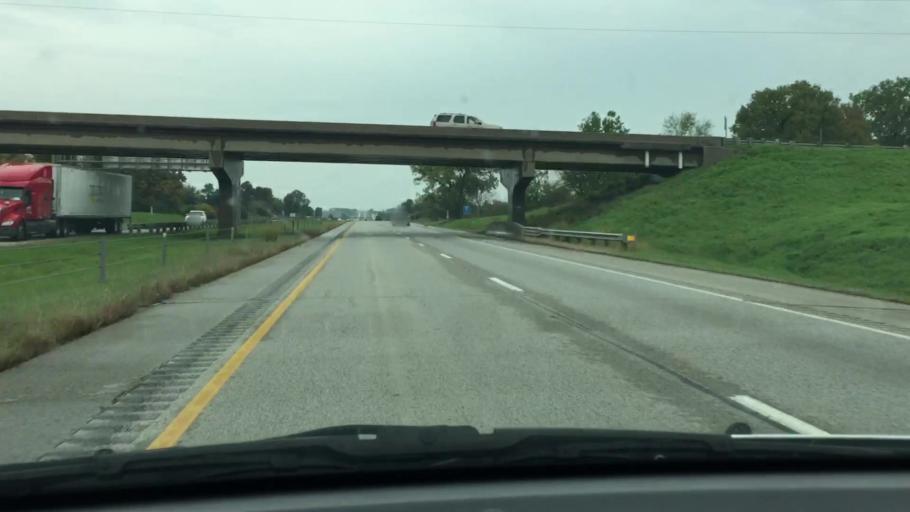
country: US
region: Iowa
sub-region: Johnson County
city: Tiffin
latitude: 41.6940
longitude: -91.6660
